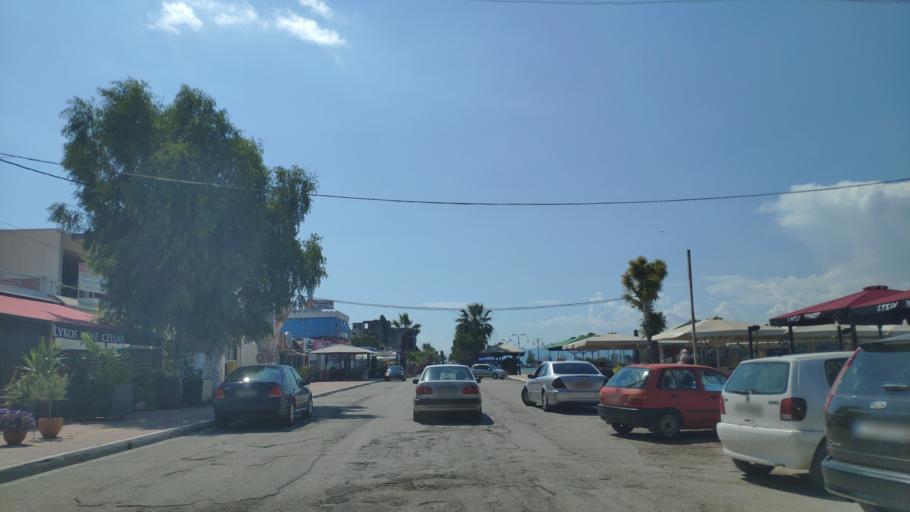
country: GR
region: Central Greece
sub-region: Nomos Evvoias
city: Eretria
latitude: 38.3913
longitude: 23.7967
